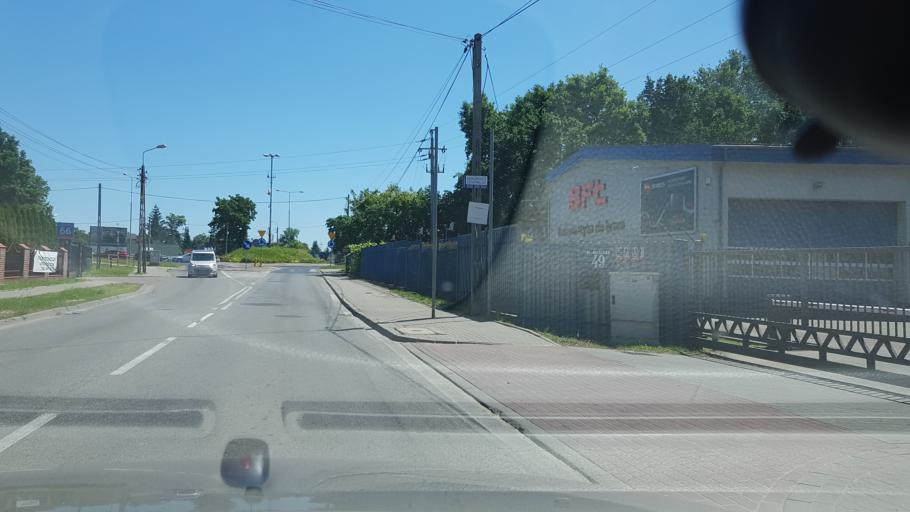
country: PL
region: Masovian Voivodeship
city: Zielonka
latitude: 52.3114
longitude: 21.1378
